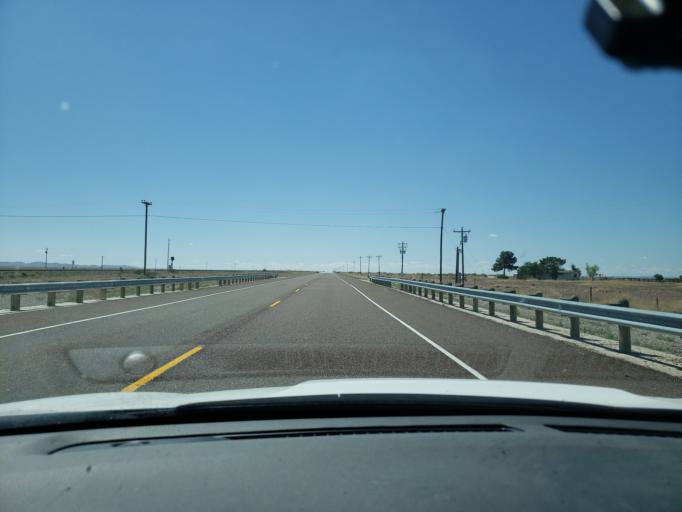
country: US
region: Texas
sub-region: Presidio County
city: Marfa
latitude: 30.5393
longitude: -104.4371
